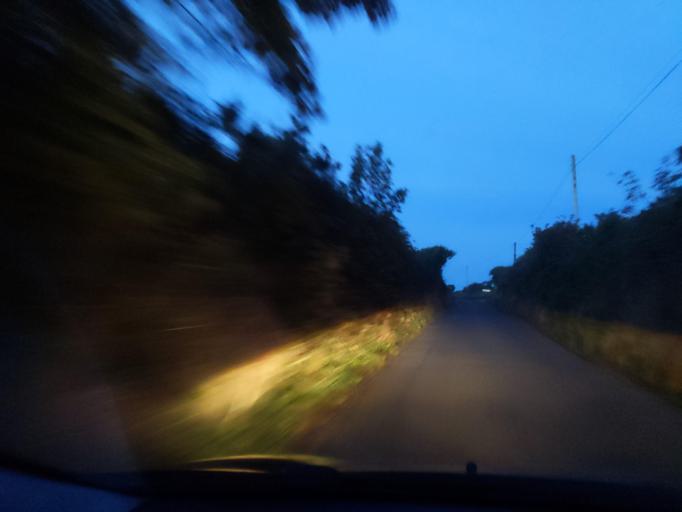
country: GB
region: England
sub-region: Cornwall
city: Camelford
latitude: 50.6977
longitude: -4.6611
